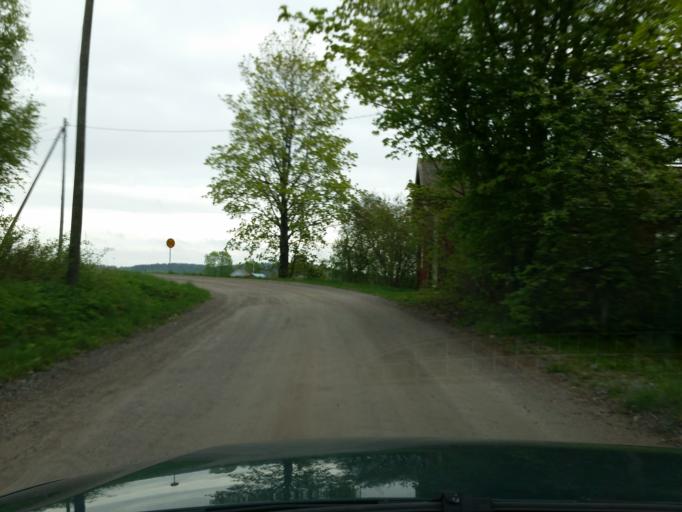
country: FI
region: Uusimaa
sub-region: Helsinki
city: Karjalohja
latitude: 60.1841
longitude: 23.6425
